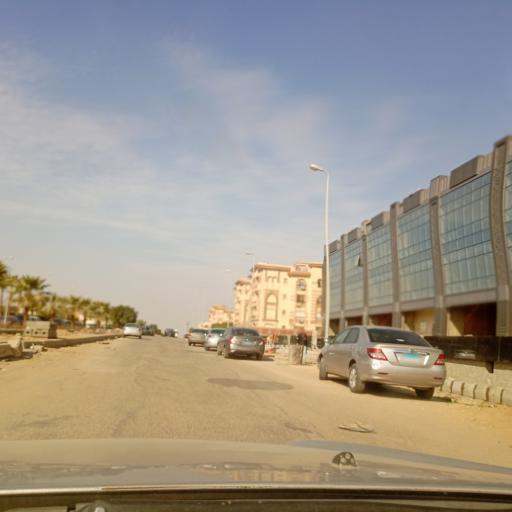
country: EG
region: Muhafazat al Qalyubiyah
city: Al Khankah
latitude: 30.0464
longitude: 31.4852
